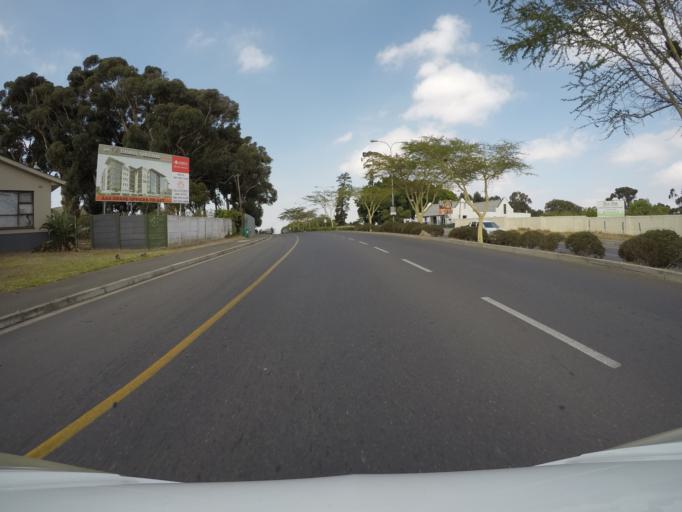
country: ZA
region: Western Cape
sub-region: City of Cape Town
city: Kraaifontein
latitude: -33.8726
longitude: 18.6429
